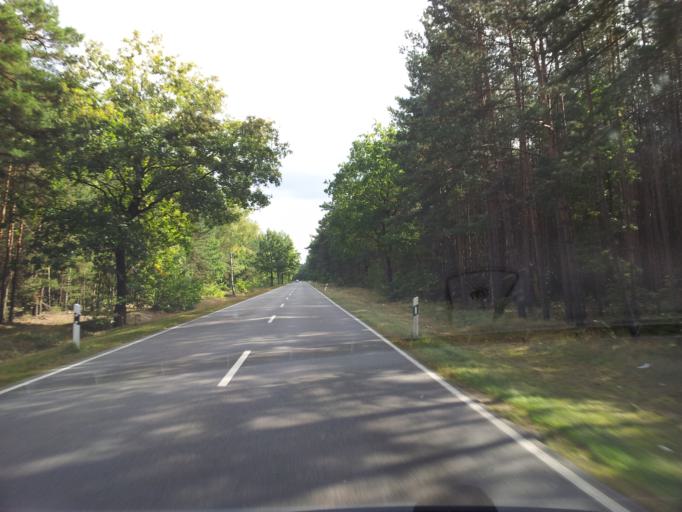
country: DE
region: Brandenburg
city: Ruhland
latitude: 51.4494
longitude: 13.8882
